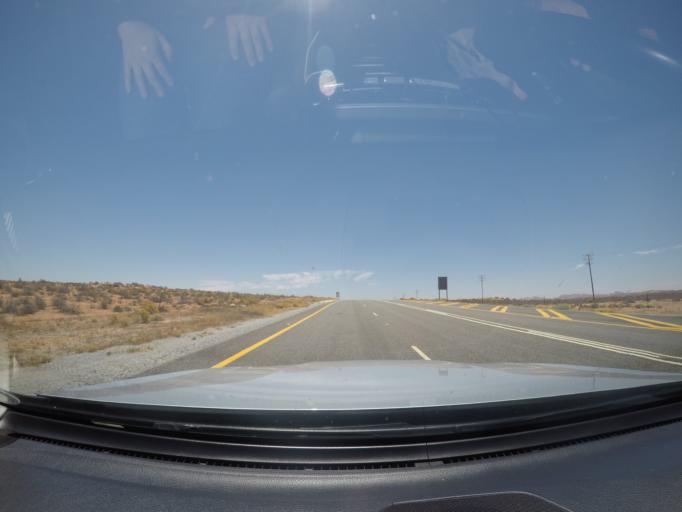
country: ZA
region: Northern Cape
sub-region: Namakwa District Municipality
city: Springbok
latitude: -29.3828
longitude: 17.7997
